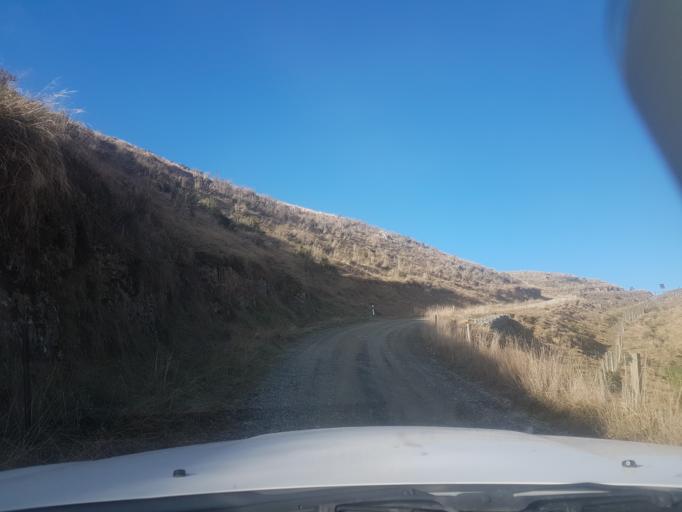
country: NZ
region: Canterbury
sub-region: Timaru District
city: Pleasant Point
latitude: -44.1750
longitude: 170.8863
